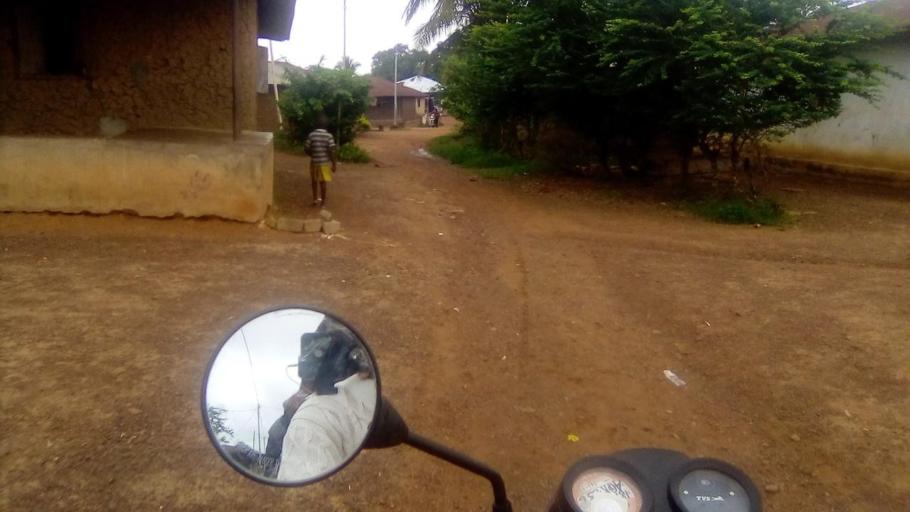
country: SL
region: Southern Province
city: Tongole
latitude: 7.4324
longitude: -11.8412
